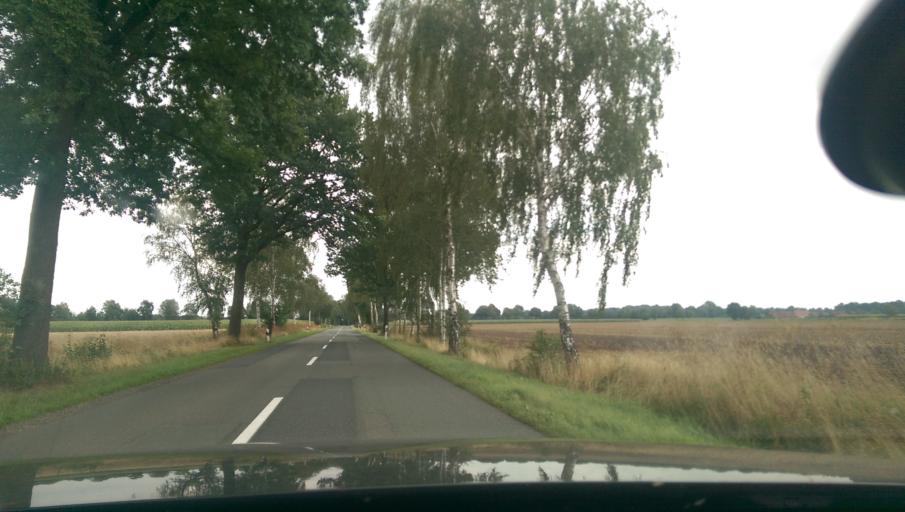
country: DE
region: Lower Saxony
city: Frankenfeld
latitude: 52.7039
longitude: 9.4704
